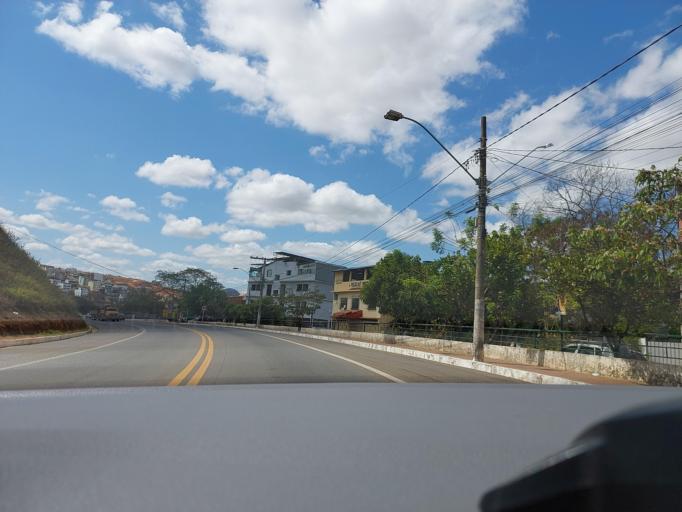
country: BR
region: Minas Gerais
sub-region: Muriae
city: Muriae
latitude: -21.1293
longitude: -42.3594
